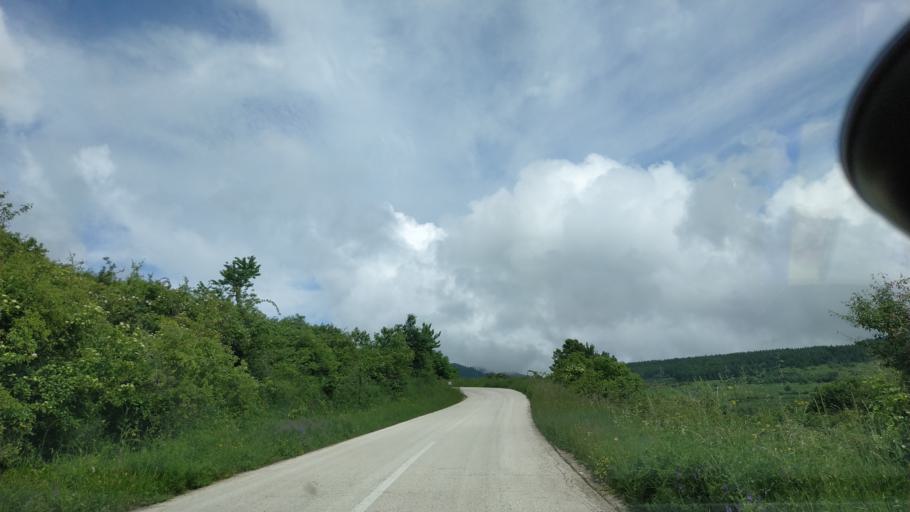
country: RS
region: Central Serbia
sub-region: Zajecarski Okrug
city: Boljevac
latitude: 43.7468
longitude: 21.9470
